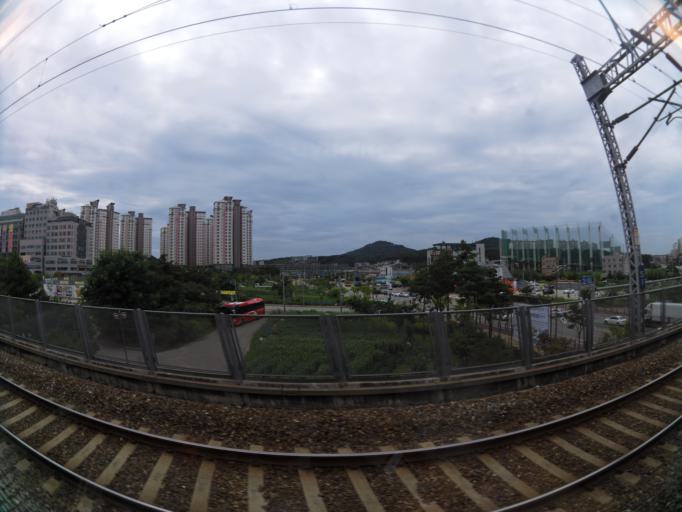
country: KR
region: Gyeonggi-do
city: Osan
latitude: 37.1881
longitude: 127.0425
